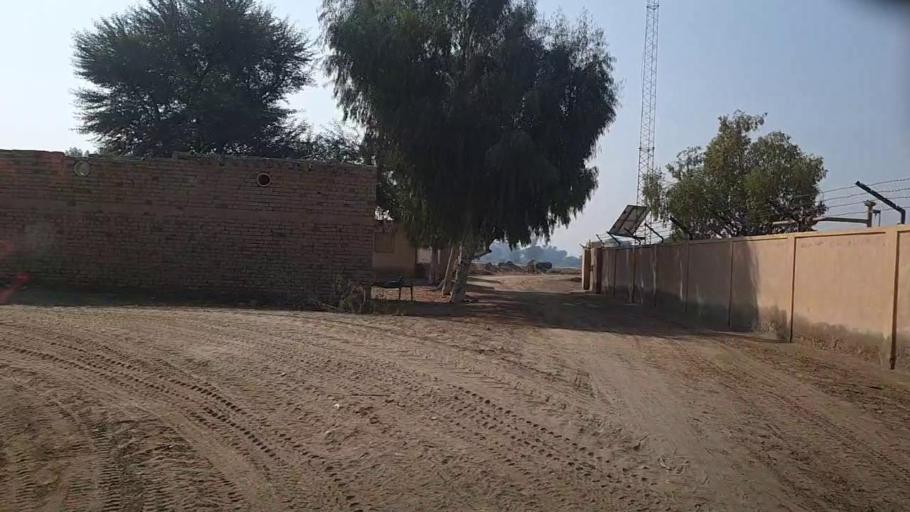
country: PK
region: Sindh
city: Bozdar
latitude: 27.2121
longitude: 68.5760
